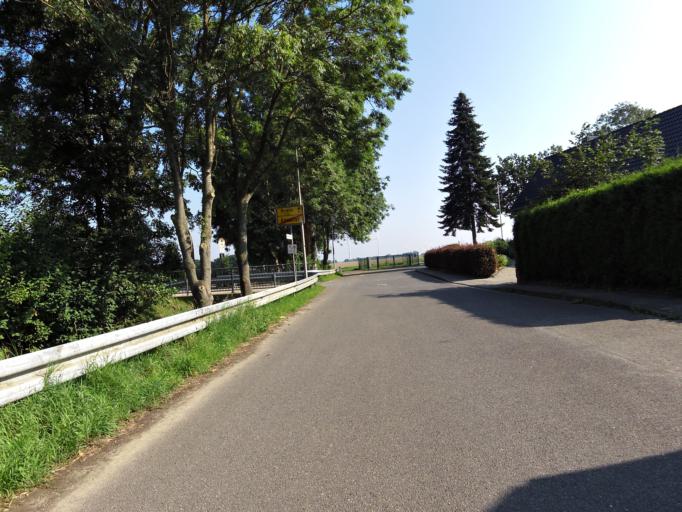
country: DE
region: North Rhine-Westphalia
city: Baesweiler
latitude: 50.9553
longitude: 6.1948
